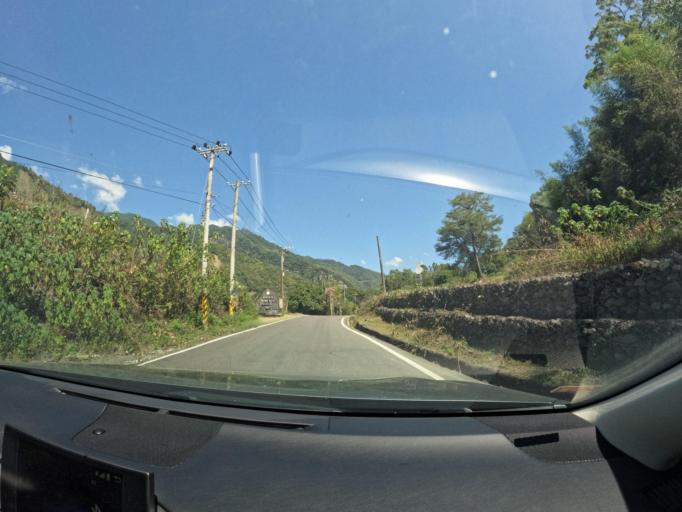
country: TW
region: Taiwan
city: Yujing
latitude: 23.2414
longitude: 120.8134
